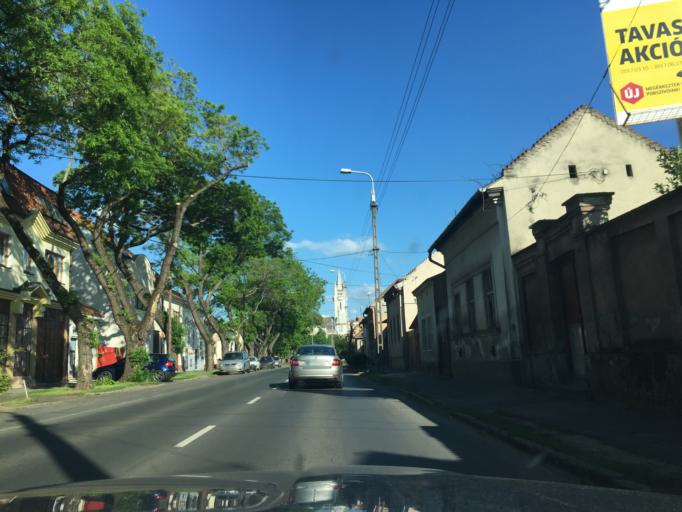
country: HU
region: Hajdu-Bihar
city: Debrecen
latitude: 47.5391
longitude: 21.6345
